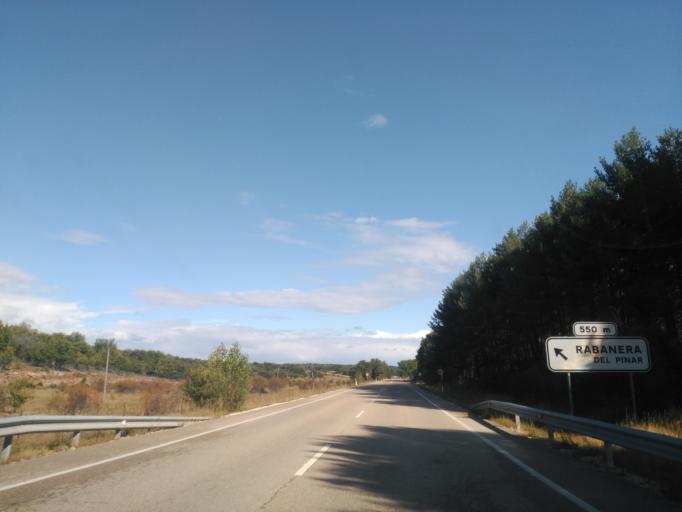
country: ES
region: Castille and Leon
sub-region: Provincia de Burgos
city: Rabanera del Pinar
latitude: 41.8861
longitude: -3.2349
